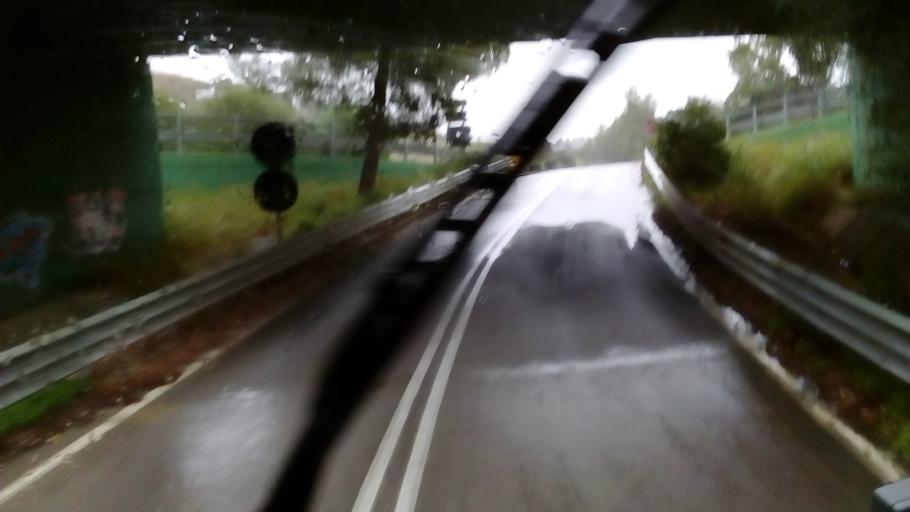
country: IT
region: Sicily
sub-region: Enna
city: Pietraperzia
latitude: 37.4926
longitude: 14.1488
